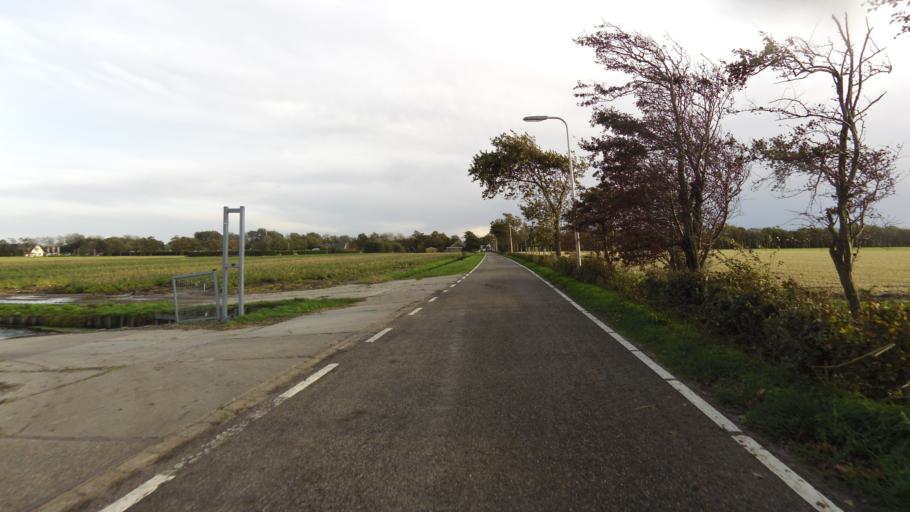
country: NL
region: South Holland
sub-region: Gemeente Noordwijkerhout
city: Noordwijkerhout
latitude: 52.2853
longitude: 4.4997
